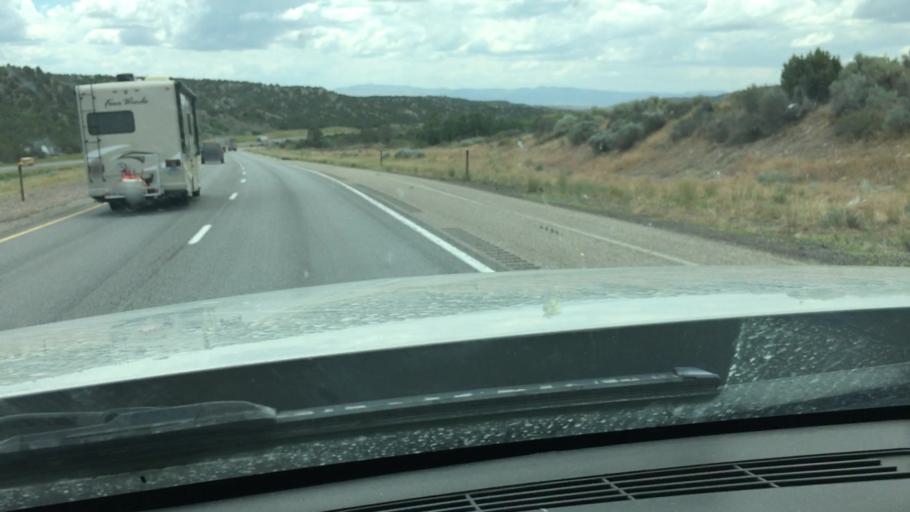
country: US
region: Utah
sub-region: Beaver County
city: Beaver
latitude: 38.4442
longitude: -112.6311
